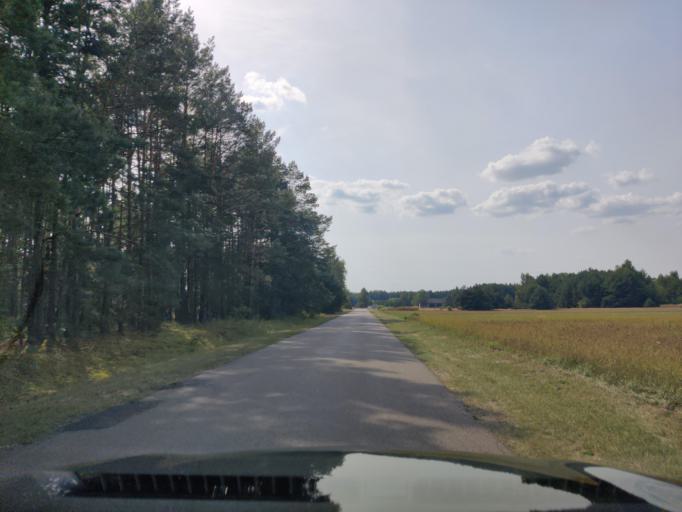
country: PL
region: Masovian Voivodeship
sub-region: Powiat wyszkowski
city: Dlugosiodlo
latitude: 52.7774
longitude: 21.4953
